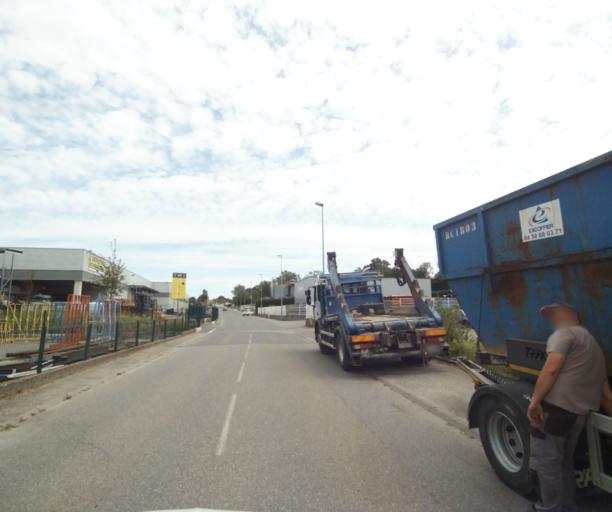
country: FR
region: Rhone-Alpes
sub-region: Departement de la Haute-Savoie
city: Anthy-sur-Leman
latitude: 46.3441
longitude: 6.4191
